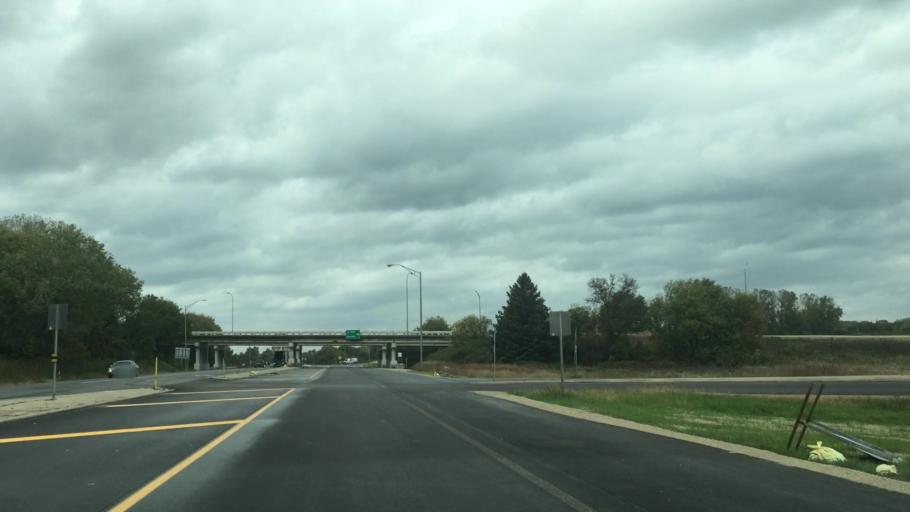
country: US
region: Minnesota
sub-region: Olmsted County
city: Eyota
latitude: 43.9498
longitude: -92.3561
